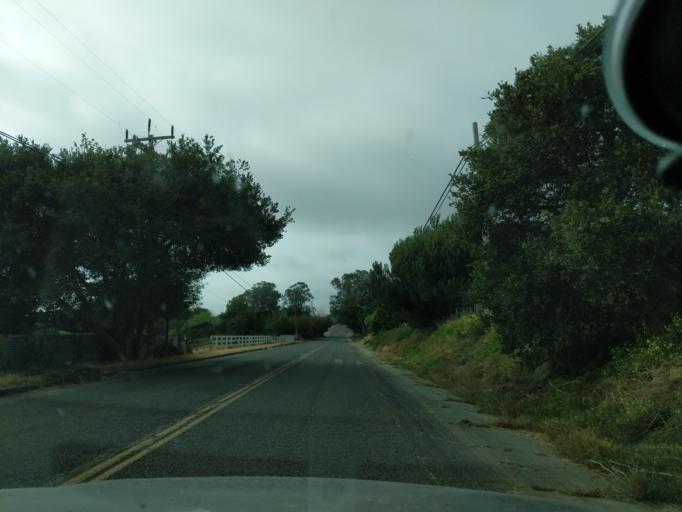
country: US
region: California
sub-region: Monterey County
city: Elkhorn
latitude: 36.8037
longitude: -121.7223
